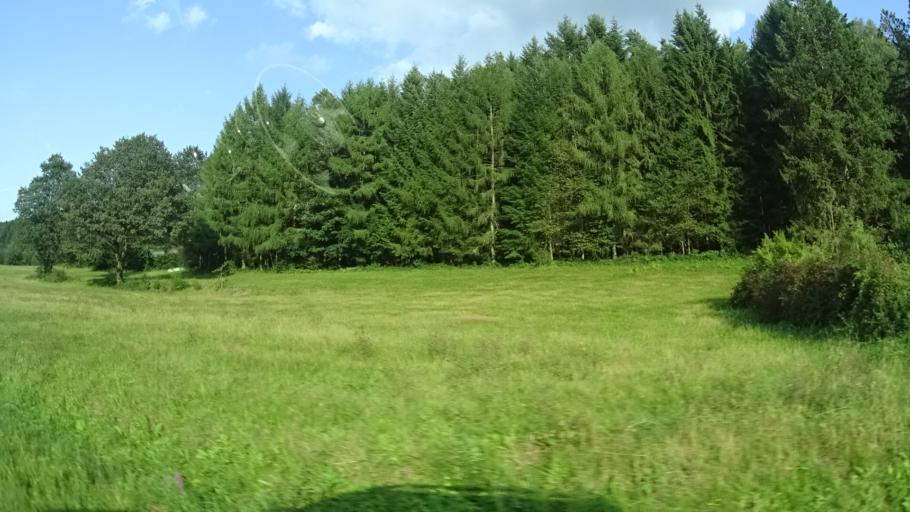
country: DE
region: Baden-Wuerttemberg
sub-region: Karlsruhe Region
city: Heddesbach
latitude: 49.5095
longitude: 8.8534
